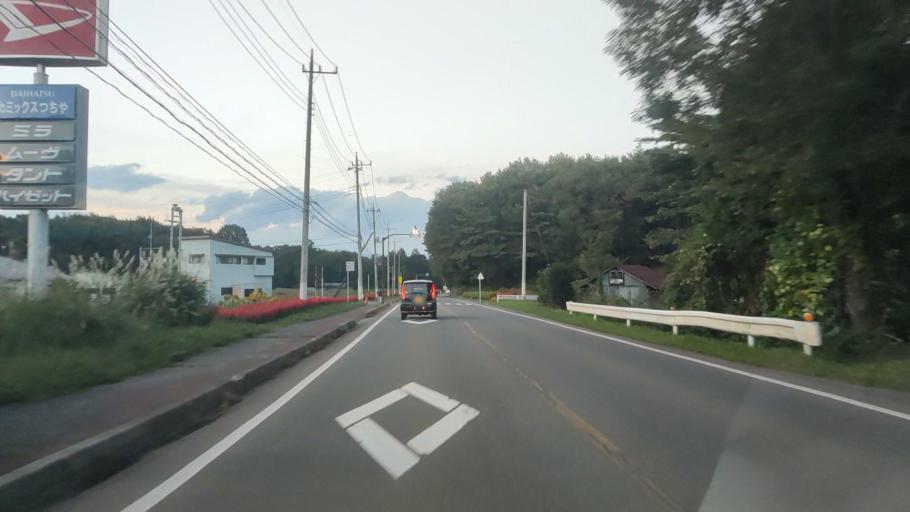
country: JP
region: Nagano
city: Komoro
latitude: 36.5090
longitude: 138.5940
